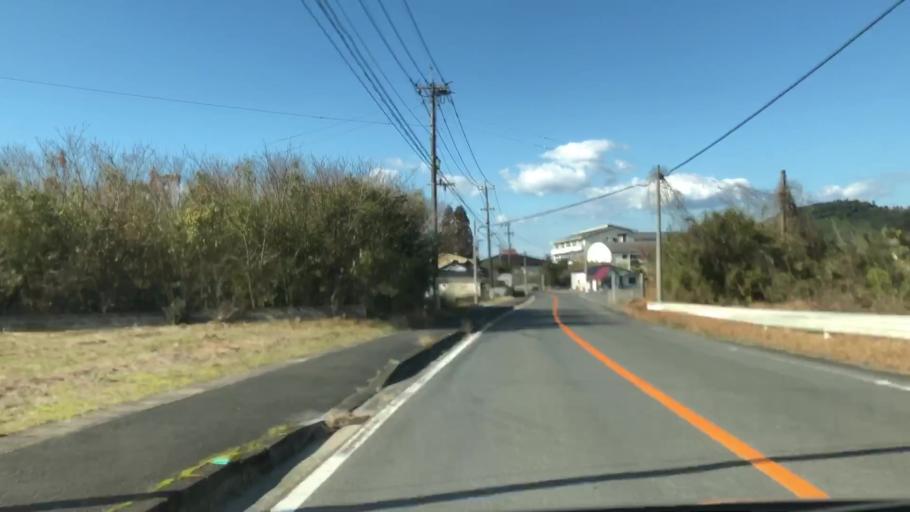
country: JP
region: Kagoshima
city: Satsumasendai
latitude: 31.7998
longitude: 130.4382
